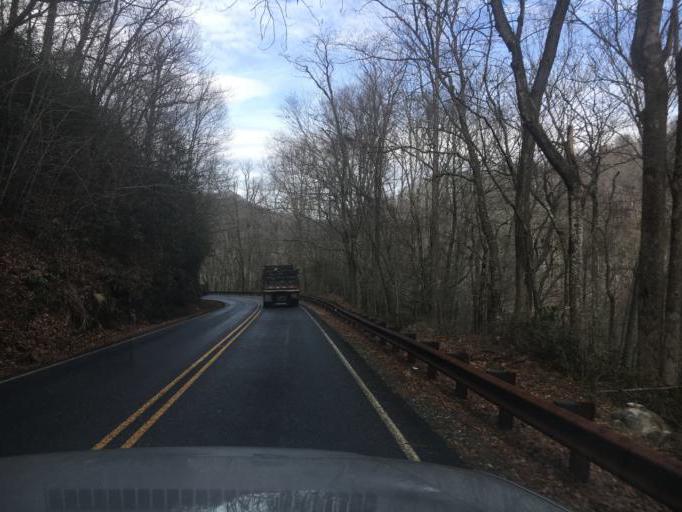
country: US
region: North Carolina
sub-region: Haywood County
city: Canton
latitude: 35.3813
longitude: -82.8110
